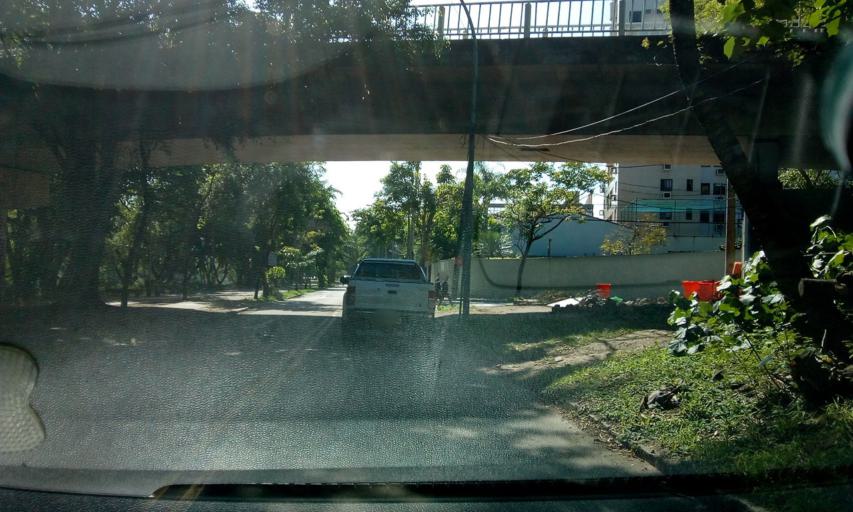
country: BR
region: Rio de Janeiro
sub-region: Rio De Janeiro
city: Rio de Janeiro
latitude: -23.0067
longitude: -43.3287
